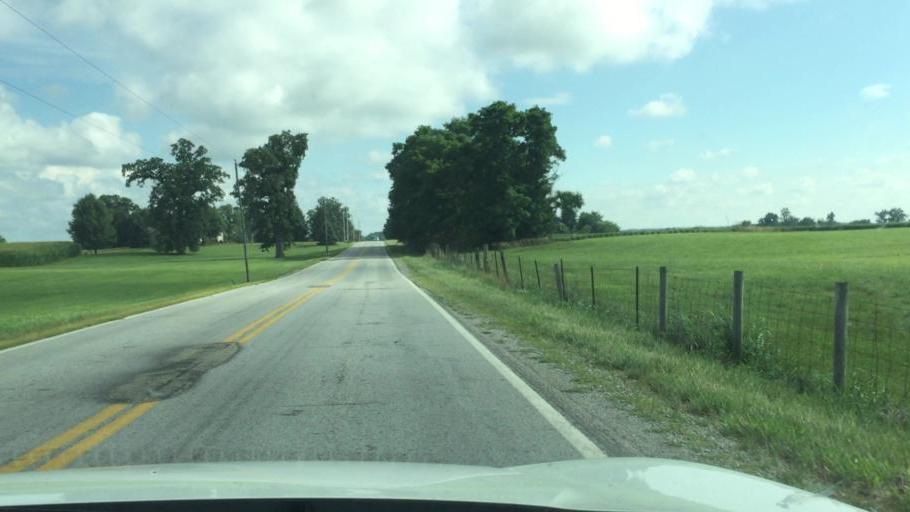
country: US
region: Ohio
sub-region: Clark County
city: Northridge
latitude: 39.9585
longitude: -83.6800
